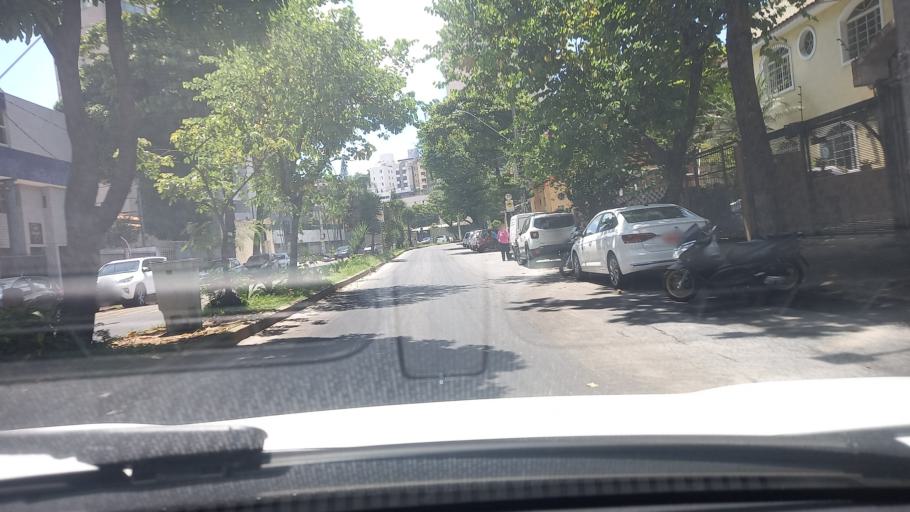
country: BR
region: Minas Gerais
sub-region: Belo Horizonte
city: Belo Horizonte
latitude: -19.9212
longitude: -43.9857
